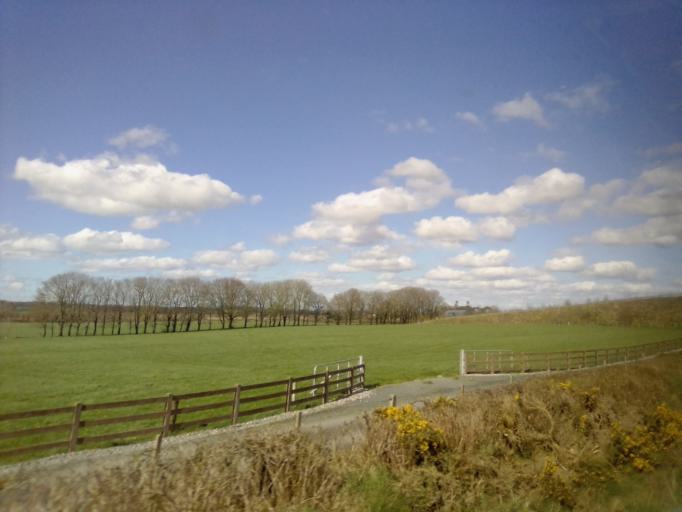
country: IE
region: Munster
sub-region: County Cork
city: Kanturk
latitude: 52.1001
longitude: -8.9617
